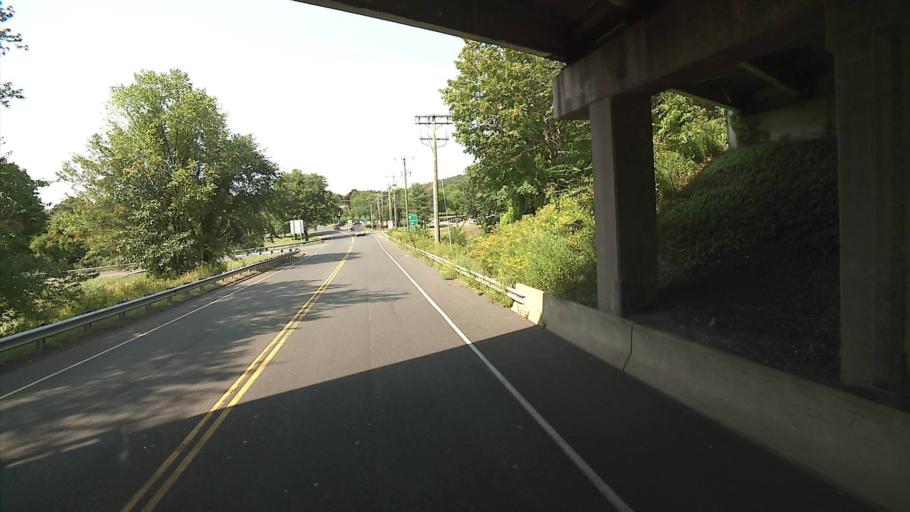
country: US
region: Connecticut
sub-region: New Haven County
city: Heritage Village
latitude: 41.4583
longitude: -73.2345
